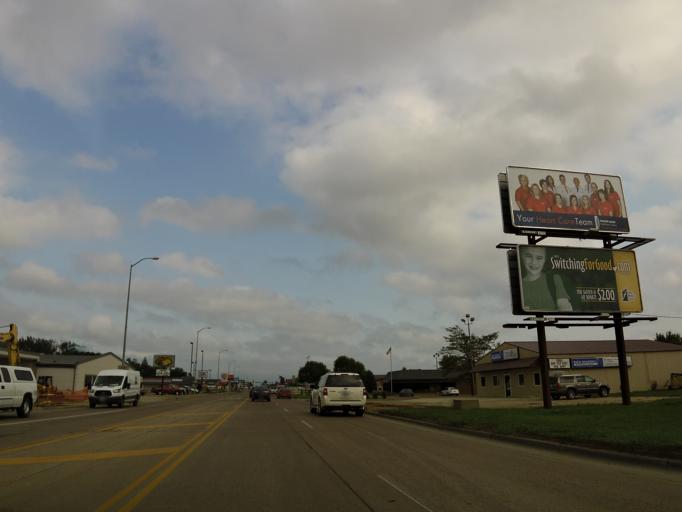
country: US
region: South Dakota
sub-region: Codington County
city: Watertown
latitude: 44.8901
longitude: -97.0999
